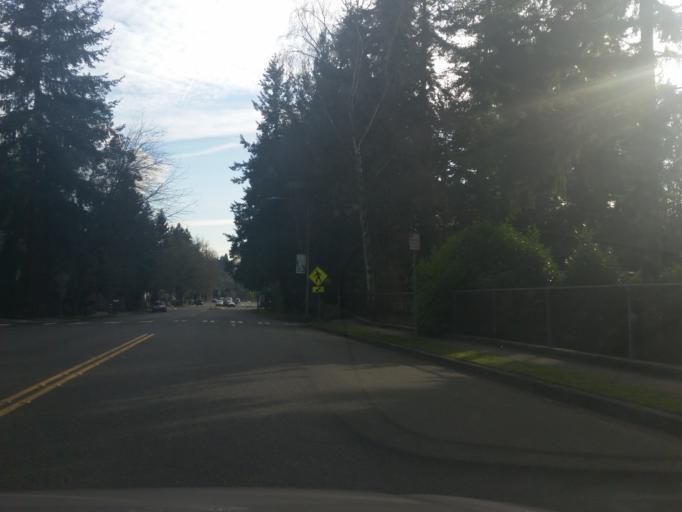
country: US
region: Washington
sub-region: King County
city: Shoreline
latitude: 47.7368
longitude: -122.3237
